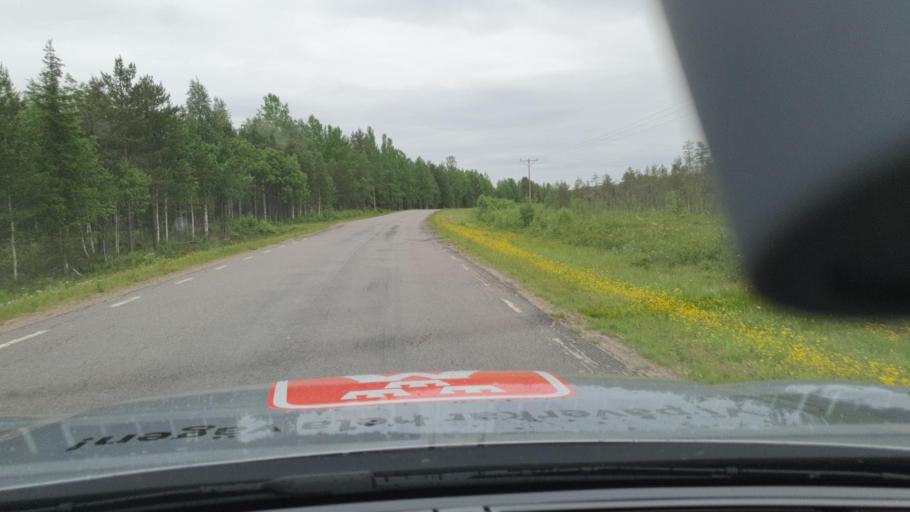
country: SE
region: Norrbotten
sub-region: Pajala Kommun
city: Pajala
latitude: 66.7453
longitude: 23.1708
